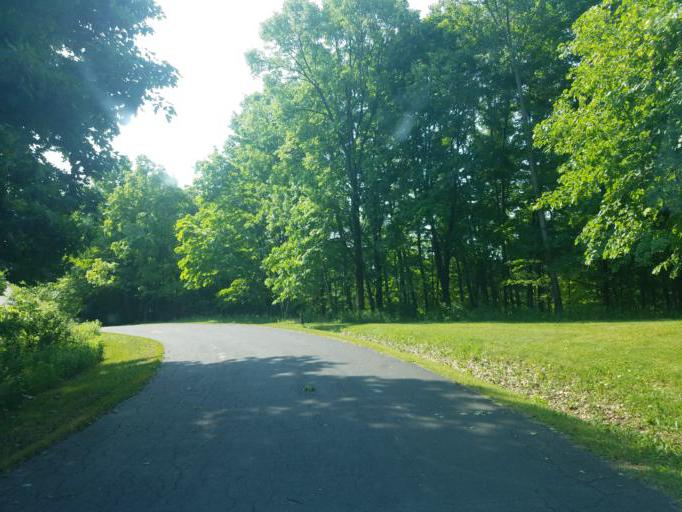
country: US
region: Wisconsin
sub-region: Monroe County
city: Cashton
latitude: 43.7018
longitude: -90.5789
